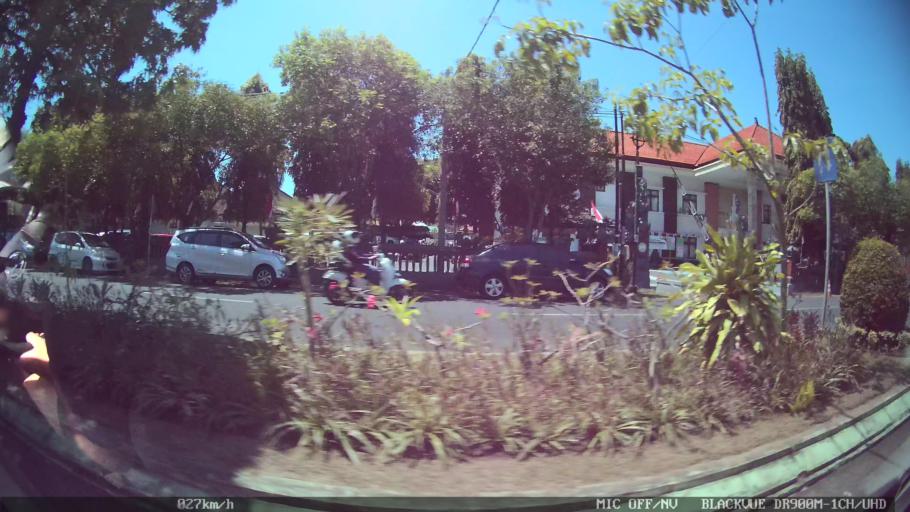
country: ID
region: Bali
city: Banjar Kaliuntu Satu
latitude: -8.1158
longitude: 115.0848
